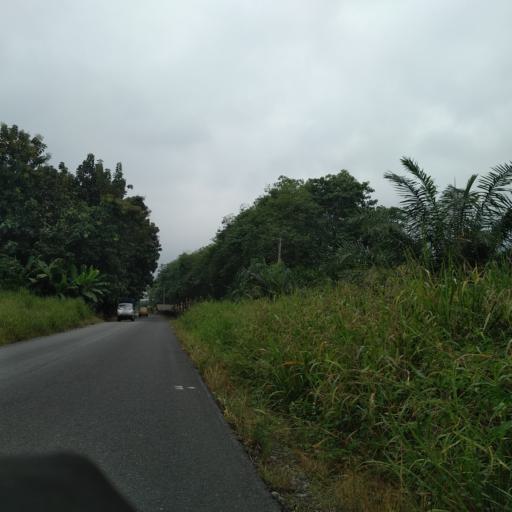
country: EC
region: Los Rios
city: Quevedo
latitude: -0.9726
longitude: -79.3556
